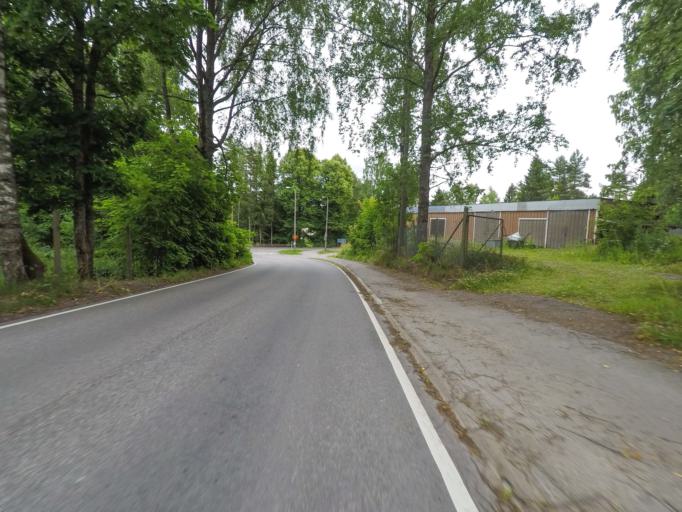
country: FI
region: Uusimaa
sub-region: Helsinki
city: Karjalohja
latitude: 60.2531
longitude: 23.7420
